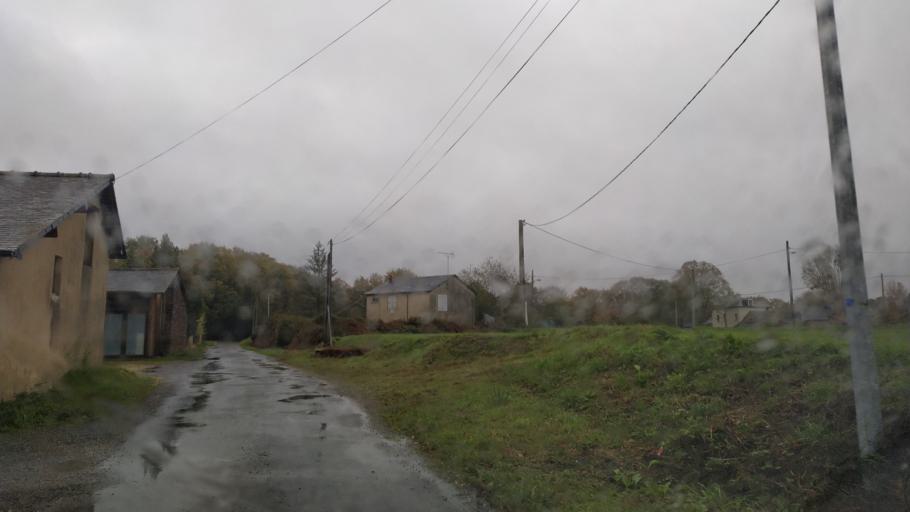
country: FR
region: Brittany
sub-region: Departement d'Ille-et-Vilaine
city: Vezin-le-Coquet
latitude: 48.0939
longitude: -1.7362
